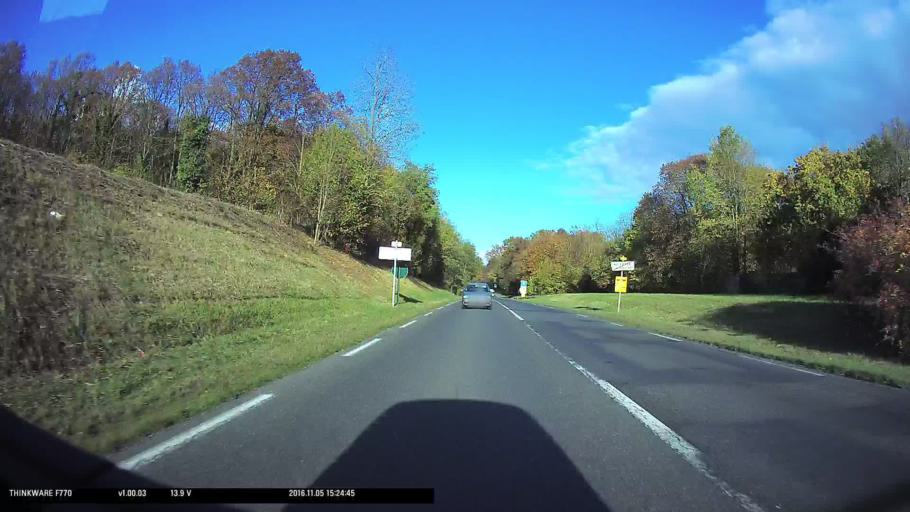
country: FR
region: Ile-de-France
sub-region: Departement du Val-d'Oise
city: Sagy
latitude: 49.0320
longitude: 1.9358
